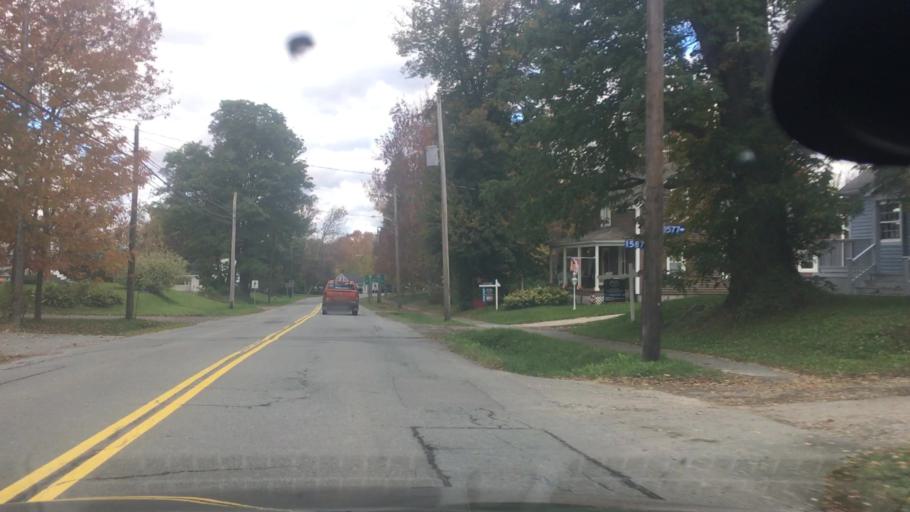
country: CA
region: Nova Scotia
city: Windsor
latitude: 44.9783
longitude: -64.1258
